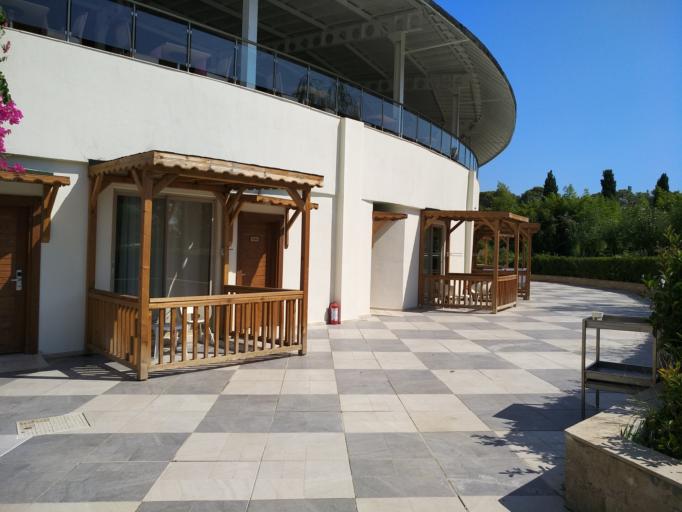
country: TR
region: Antalya
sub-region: Kemer
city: Goeynuek
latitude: 36.6660
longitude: 30.5596
